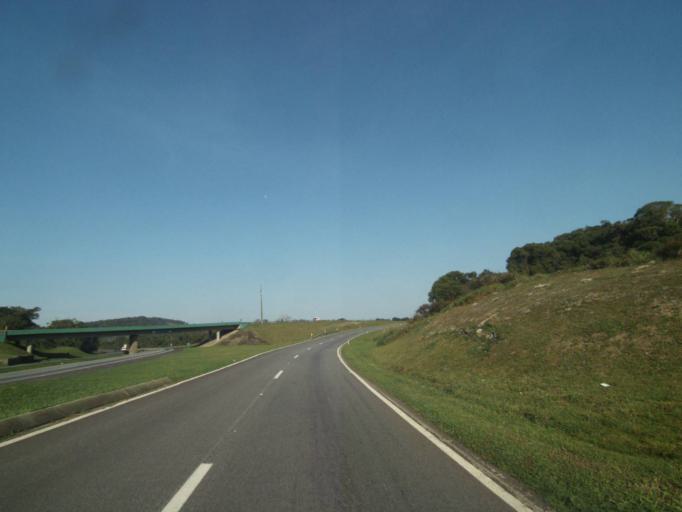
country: BR
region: Parana
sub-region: Paranagua
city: Paranagua
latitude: -25.5682
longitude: -48.6167
